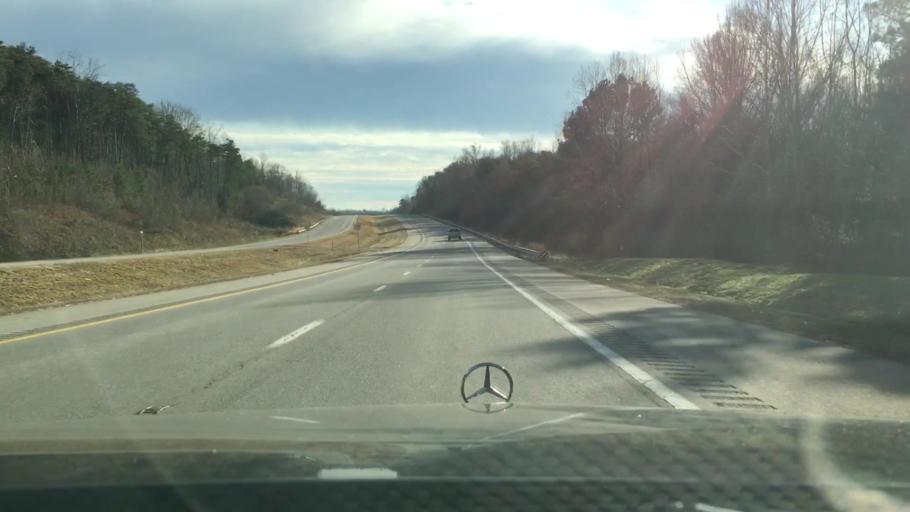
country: US
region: Virginia
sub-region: City of Danville
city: Danville
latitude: 36.6327
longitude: -79.3648
